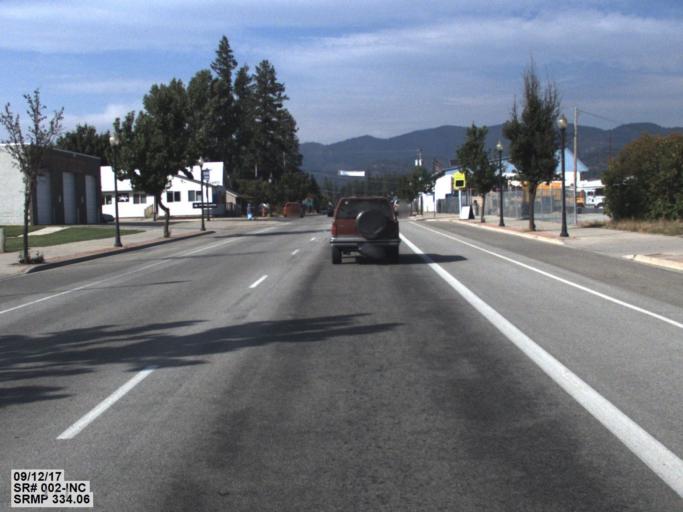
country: US
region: Washington
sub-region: Pend Oreille County
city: Newport
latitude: 48.1795
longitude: -117.0426
